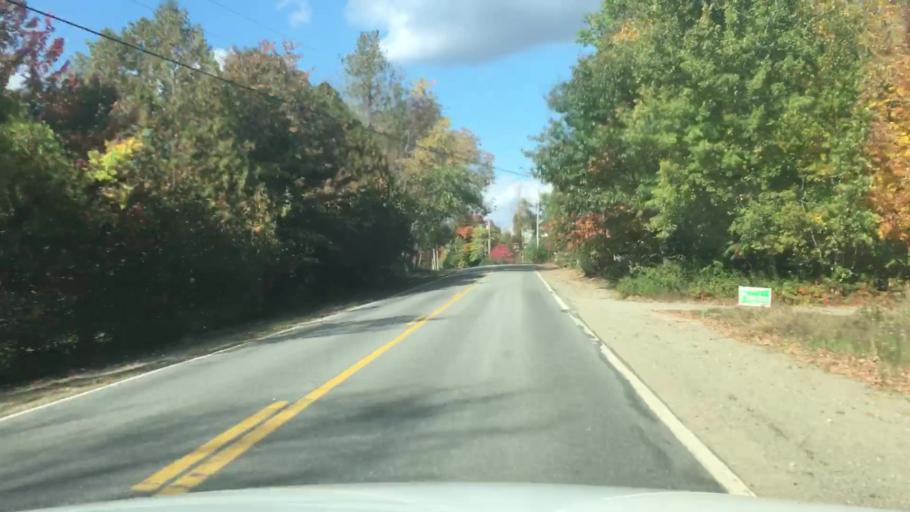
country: US
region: Maine
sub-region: Knox County
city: Union
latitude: 44.1842
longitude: -69.2603
